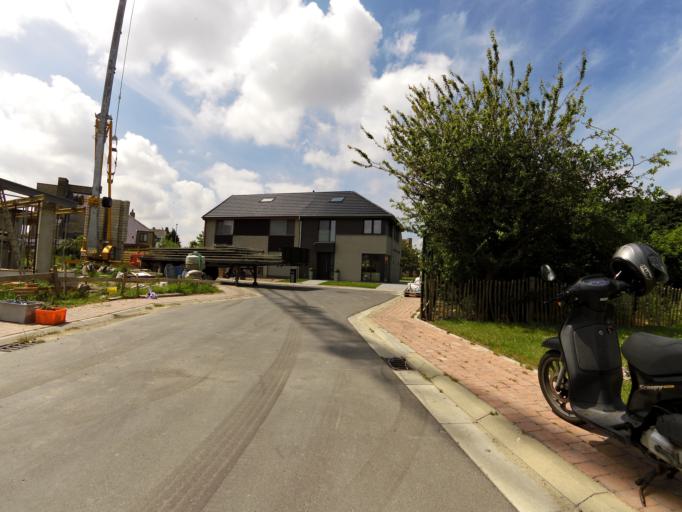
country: BE
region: Flanders
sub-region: Provincie West-Vlaanderen
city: Bredene
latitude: 51.2011
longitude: 2.9701
